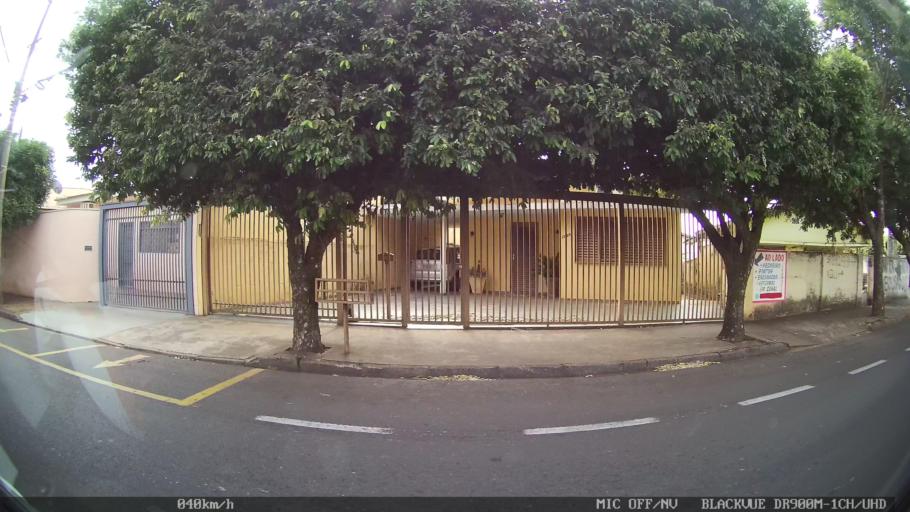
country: BR
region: Sao Paulo
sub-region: Sao Jose Do Rio Preto
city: Sao Jose do Rio Preto
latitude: -20.8190
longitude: -49.3558
